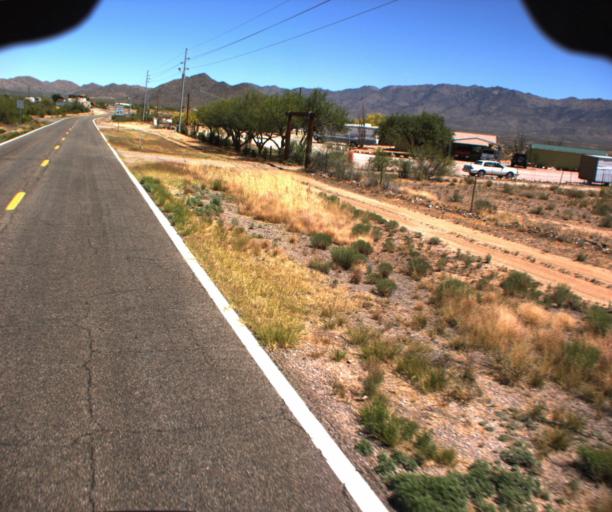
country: US
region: Arizona
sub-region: Yavapai County
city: Congress
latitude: 34.1505
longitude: -112.8432
